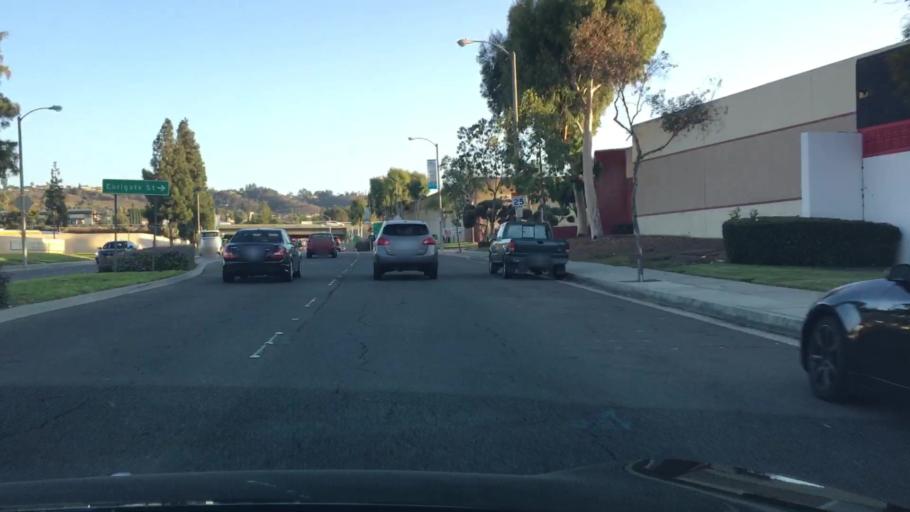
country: US
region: California
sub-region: Los Angeles County
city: Walnut
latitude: 34.0011
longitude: -117.8553
